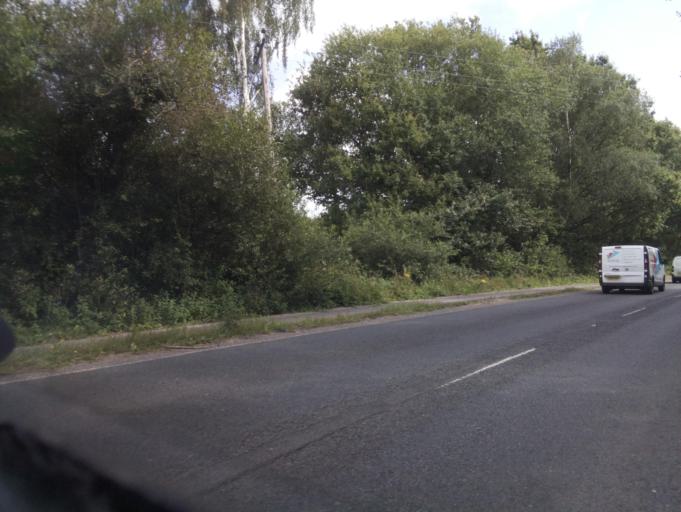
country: GB
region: England
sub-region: Hampshire
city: Marchwood
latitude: 50.8715
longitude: -1.4391
